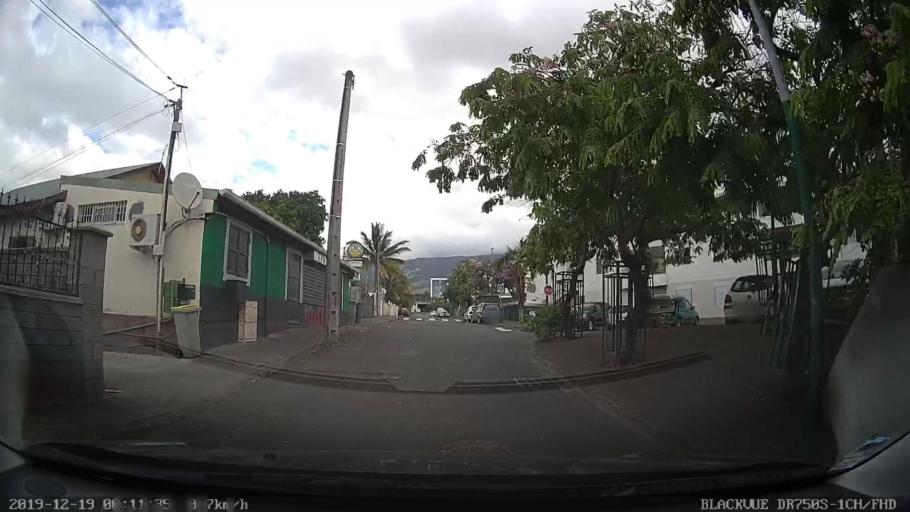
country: RE
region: Reunion
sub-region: Reunion
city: Sainte-Marie
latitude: -20.9000
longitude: 55.5029
